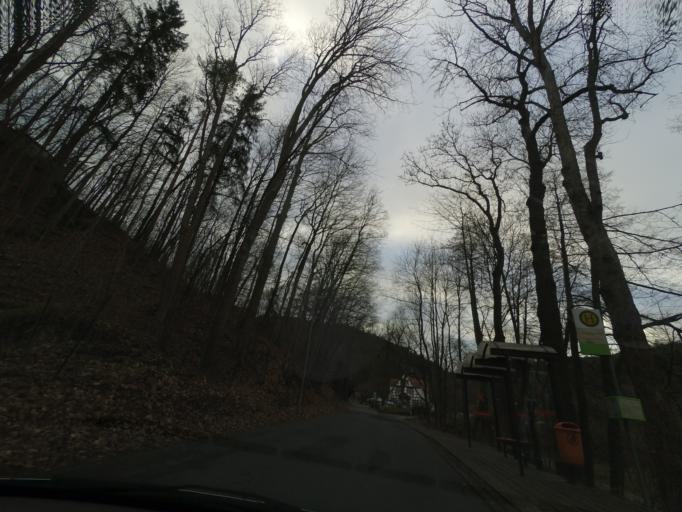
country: DE
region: Thuringia
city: Saalfeld
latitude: 50.6360
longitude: 11.3434
